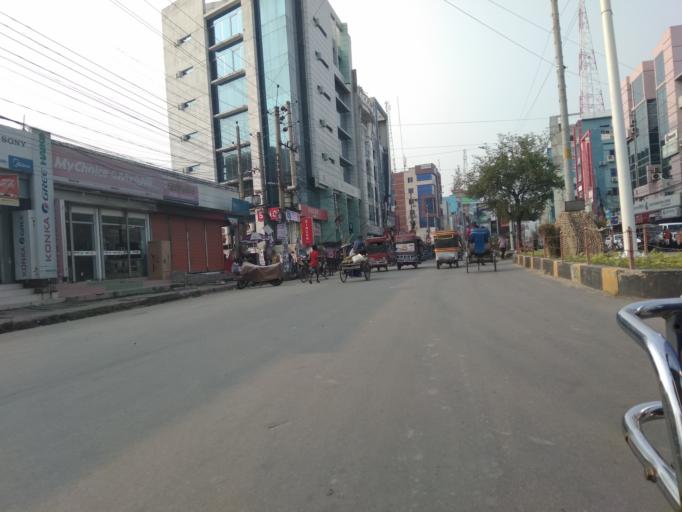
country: BD
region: Khulna
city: Khulna
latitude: 22.8177
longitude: 89.5534
